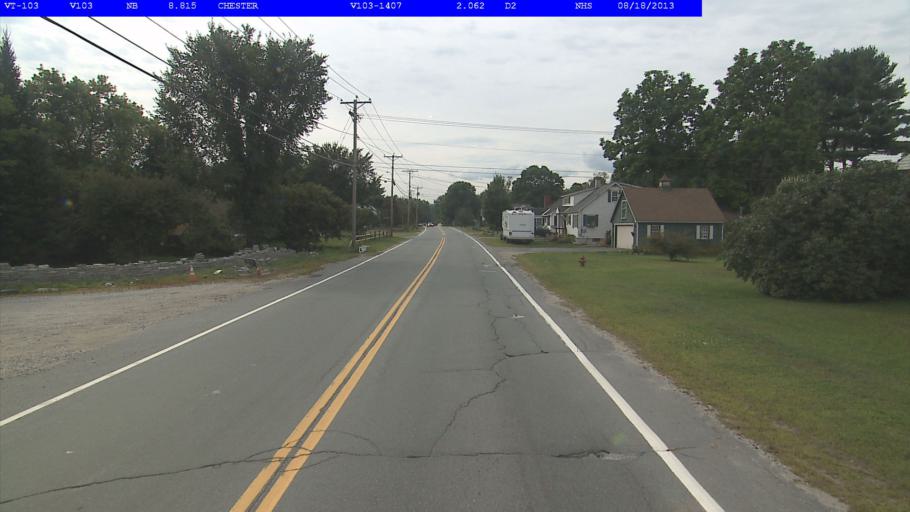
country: US
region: Vermont
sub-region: Windsor County
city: Chester
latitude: 43.2561
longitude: -72.5805
